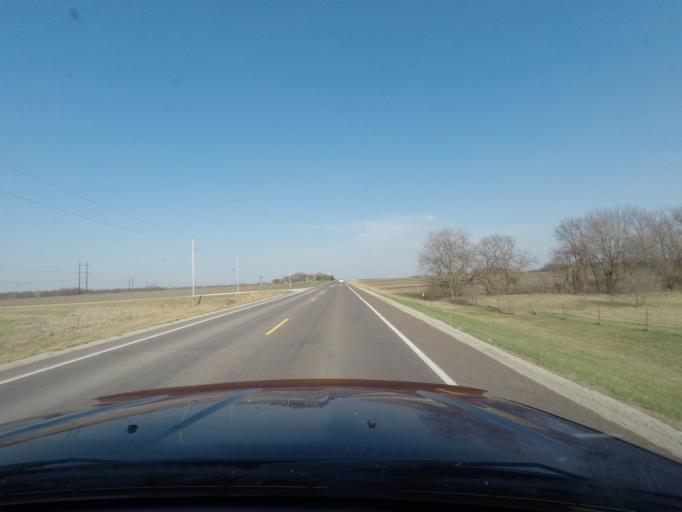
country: US
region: Kansas
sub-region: Douglas County
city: Lawrence
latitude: 39.0006
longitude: -95.3265
